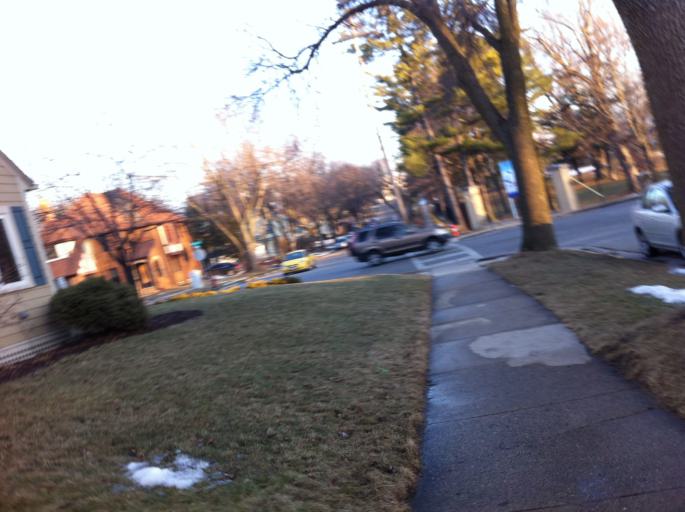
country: US
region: Wisconsin
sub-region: Dane County
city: Madison
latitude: 43.0635
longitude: -89.4224
